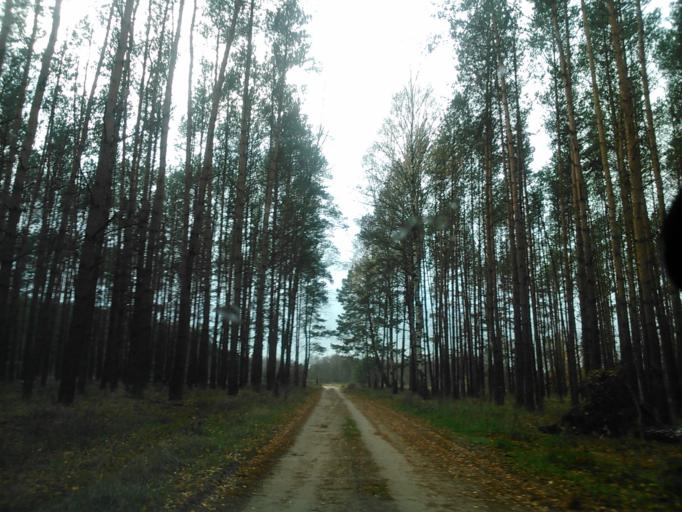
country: PL
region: Kujawsko-Pomorskie
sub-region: Powiat golubsko-dobrzynski
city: Golub-Dobrzyn
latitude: 53.1280
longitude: 19.1243
